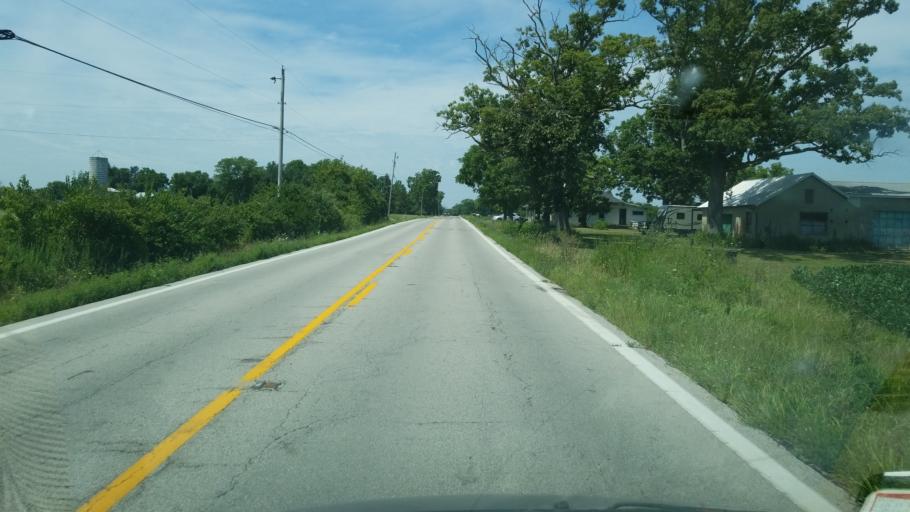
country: US
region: Ohio
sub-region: Madison County
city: West Jefferson
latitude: 39.8560
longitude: -83.2334
